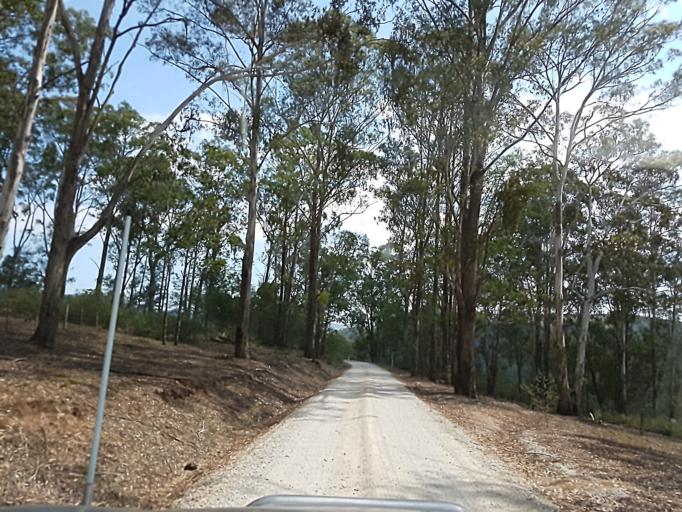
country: AU
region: Victoria
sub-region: East Gippsland
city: Lakes Entrance
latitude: -37.4774
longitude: 148.2432
